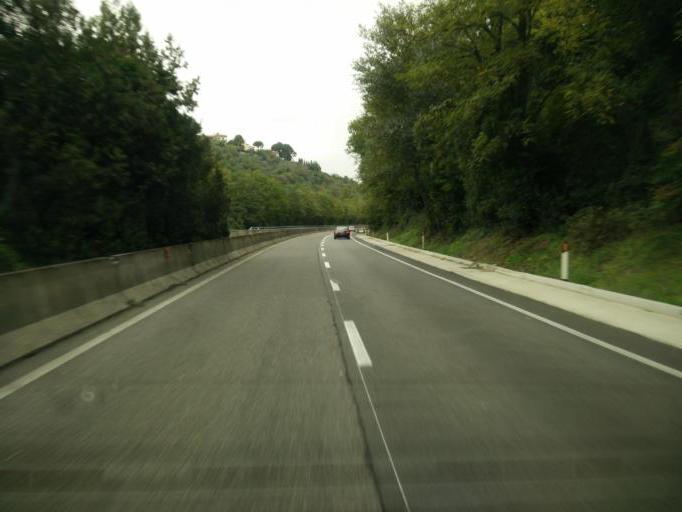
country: IT
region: Tuscany
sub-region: Province of Florence
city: San Casciano in Val di Pesa
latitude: 43.6562
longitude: 11.1967
